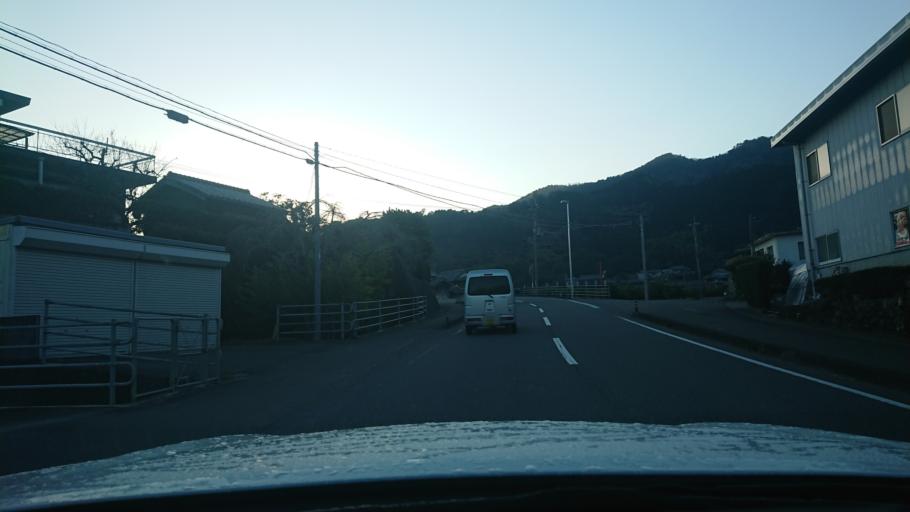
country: JP
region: Tokushima
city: Komatsushimacho
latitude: 33.9491
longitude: 134.5543
